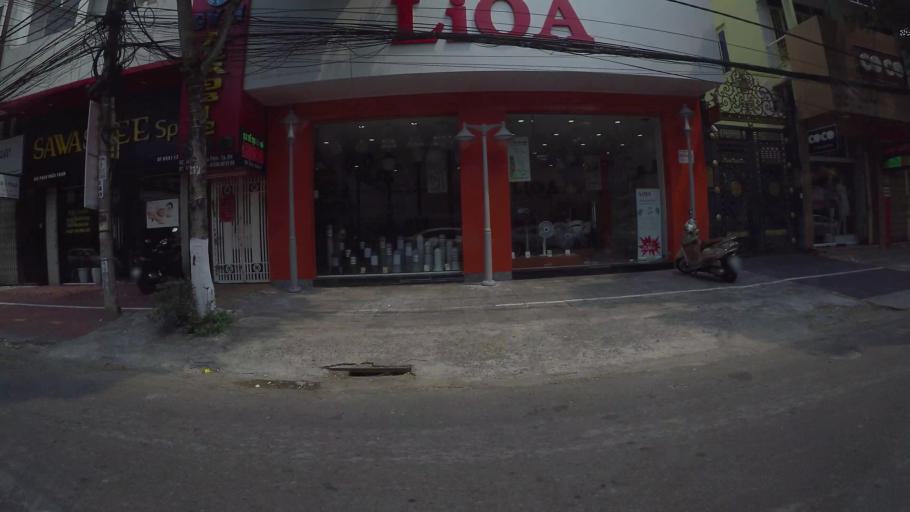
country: VN
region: Da Nang
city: Da Nang
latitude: 16.0574
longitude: 108.2190
